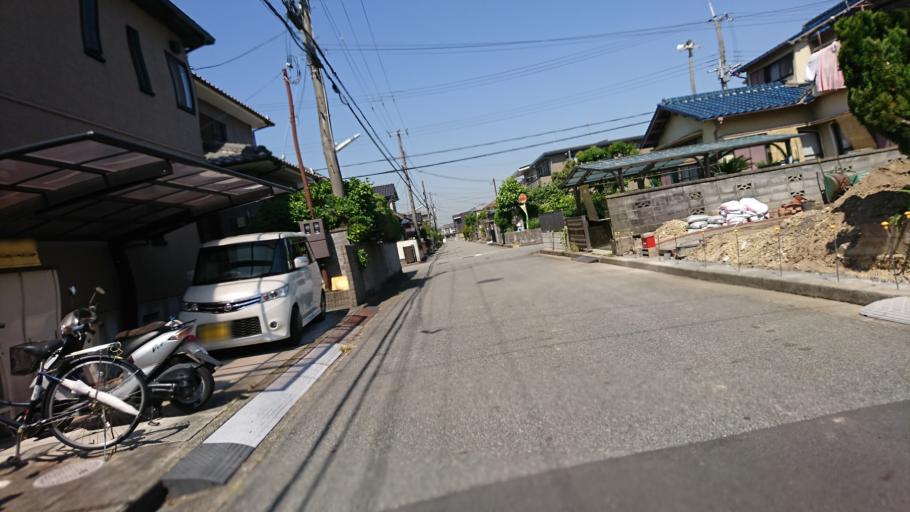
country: JP
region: Hyogo
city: Kakogawacho-honmachi
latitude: 34.7537
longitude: 134.8689
